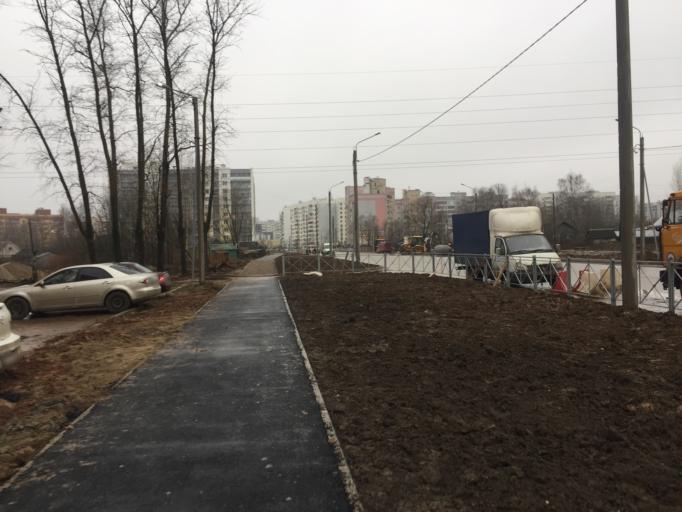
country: RU
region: Jaroslavl
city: Yaroslavl
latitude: 57.6982
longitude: 39.7870
